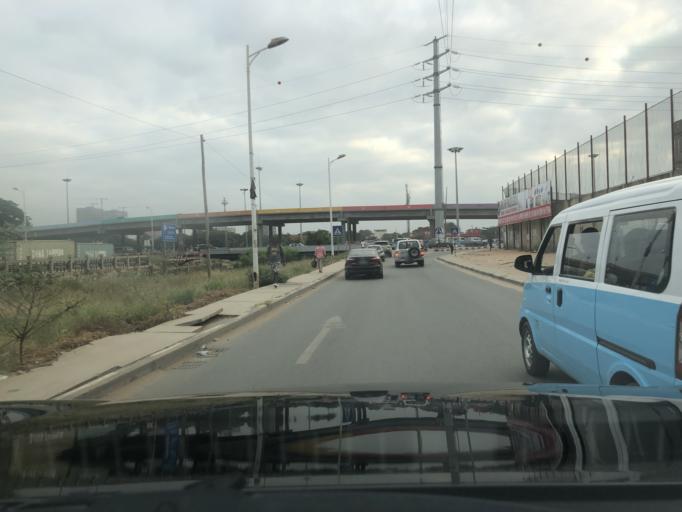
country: AO
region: Luanda
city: Luanda
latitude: -8.8357
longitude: 13.2555
